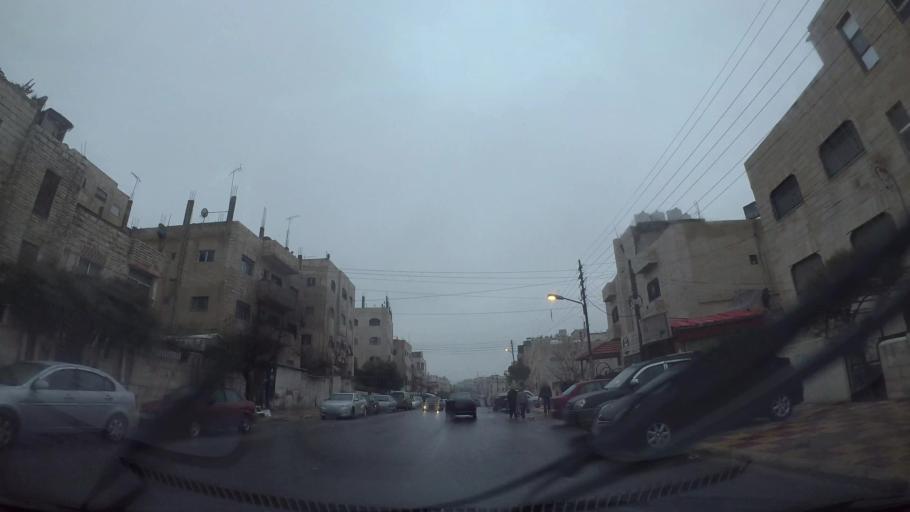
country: JO
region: Amman
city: Amman
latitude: 31.9734
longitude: 35.9208
